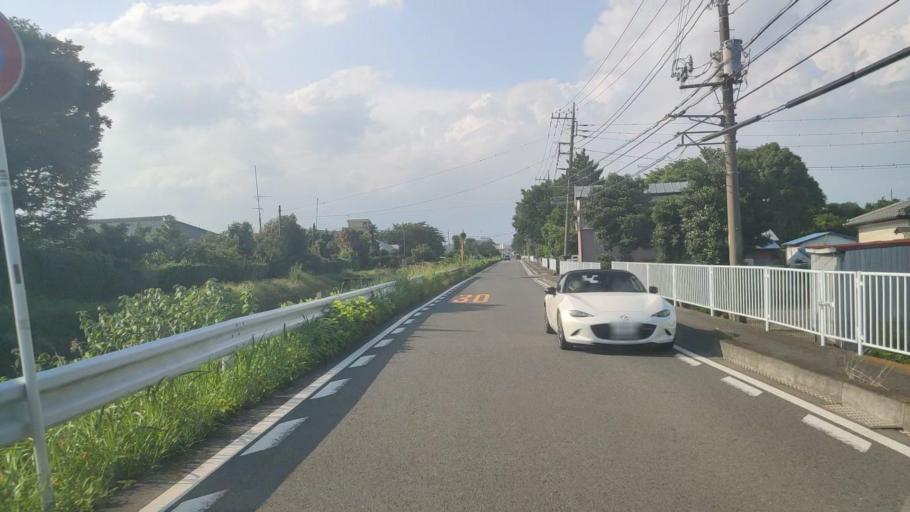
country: JP
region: Kanagawa
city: Isehara
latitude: 35.3864
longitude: 139.3387
